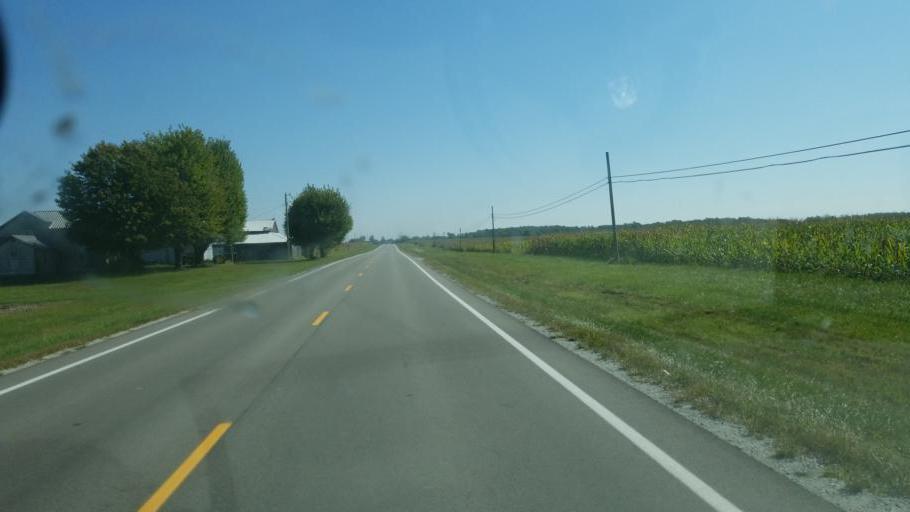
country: US
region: Ohio
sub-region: Hardin County
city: Kenton
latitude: 40.6429
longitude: -83.4853
